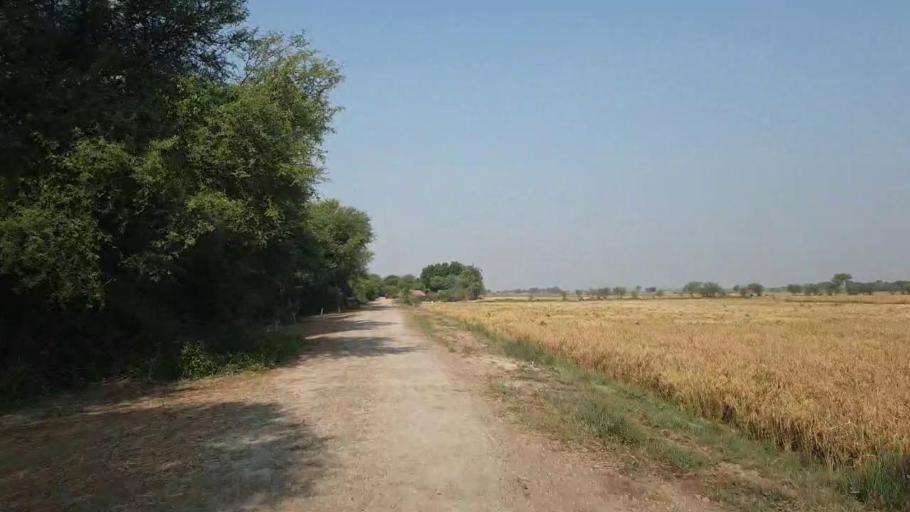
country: PK
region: Sindh
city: Matli
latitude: 24.9796
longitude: 68.6180
